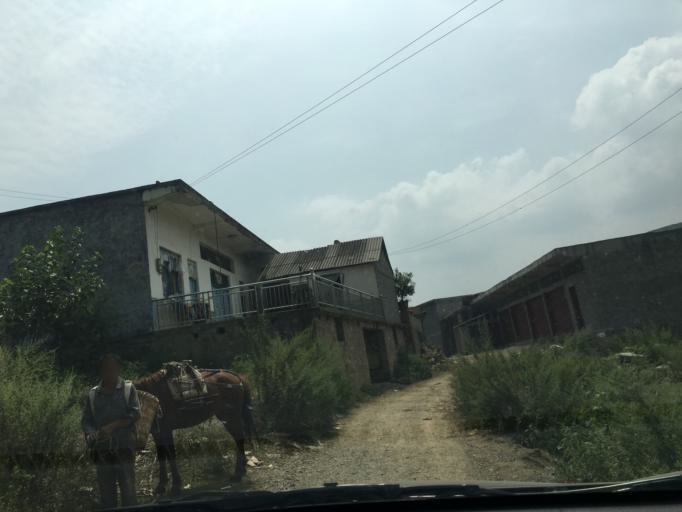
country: CN
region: Guizhou Sheng
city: Anshun
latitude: 25.5974
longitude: 105.6697
